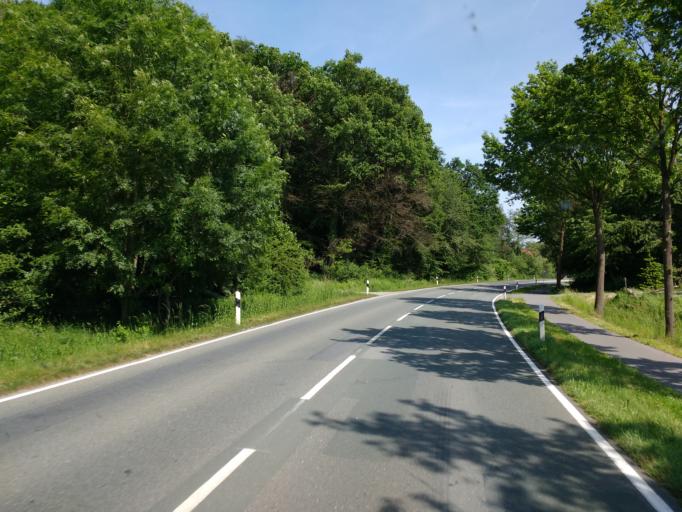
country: DE
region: Lower Saxony
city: Belm
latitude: 52.3091
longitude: 8.1166
